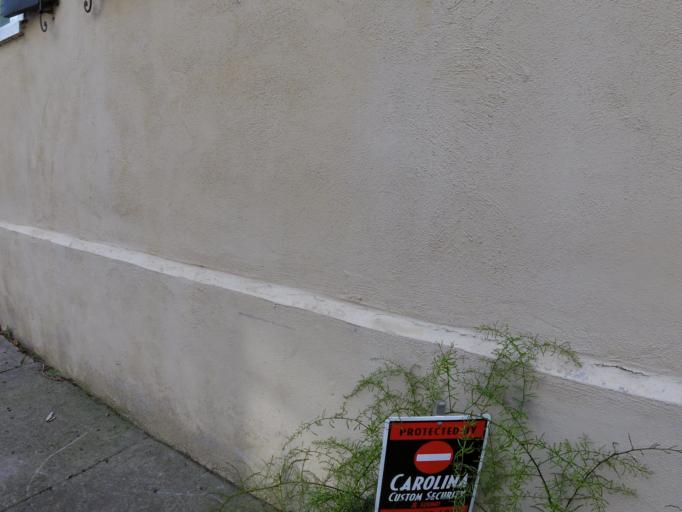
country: US
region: South Carolina
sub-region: Charleston County
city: Charleston
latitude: 32.7797
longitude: -79.9356
